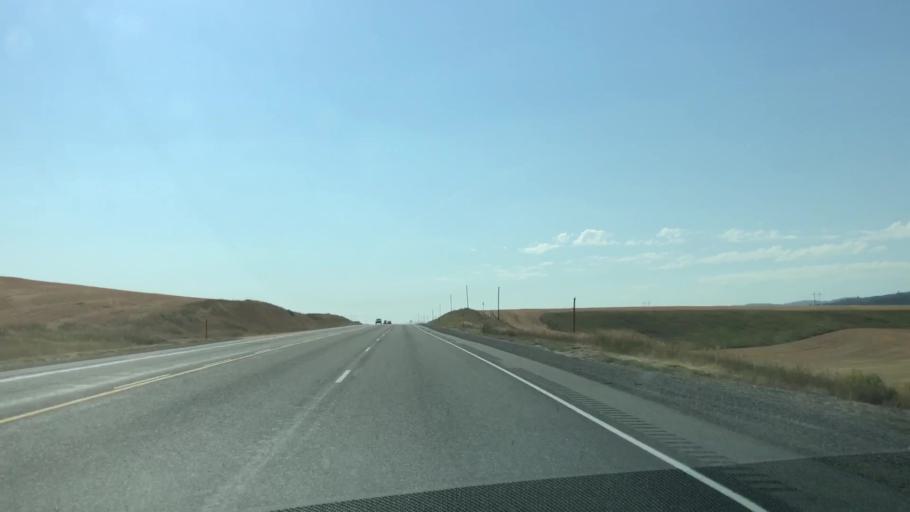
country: US
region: Idaho
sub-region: Teton County
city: Victor
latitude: 43.5313
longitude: -111.5054
